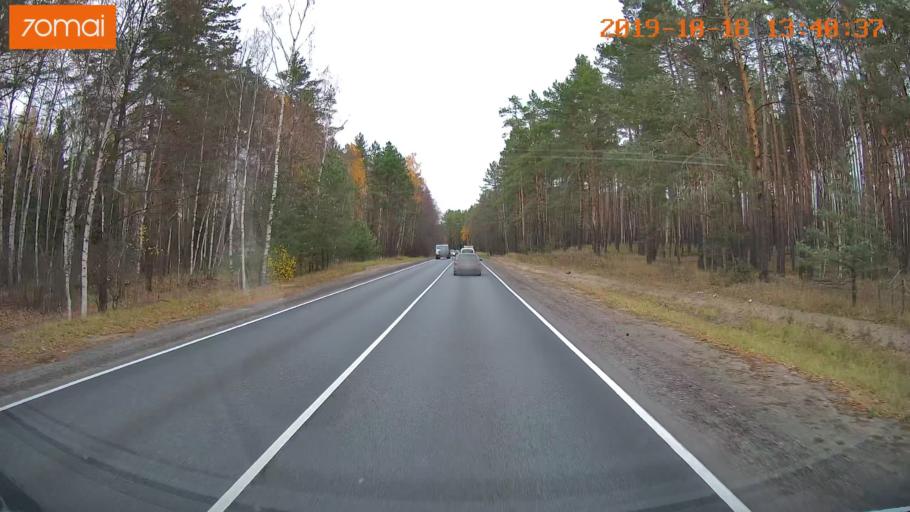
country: RU
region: Rjazan
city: Solotcha
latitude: 54.9116
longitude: 39.9978
